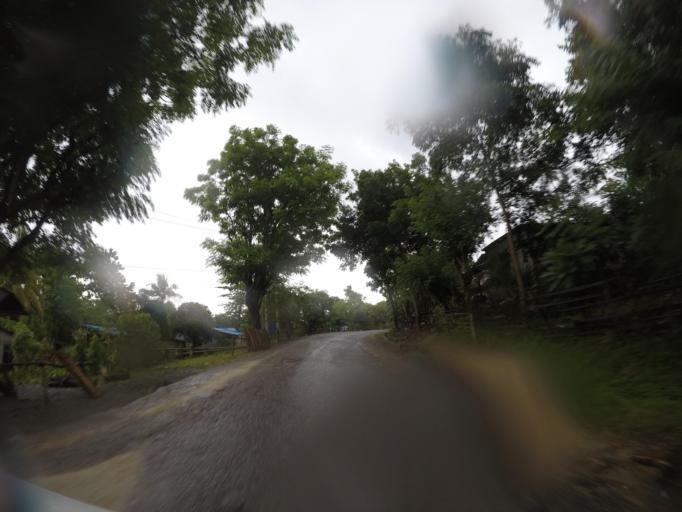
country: TL
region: Bobonaro
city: Maliana
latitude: -8.9609
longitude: 125.0289
